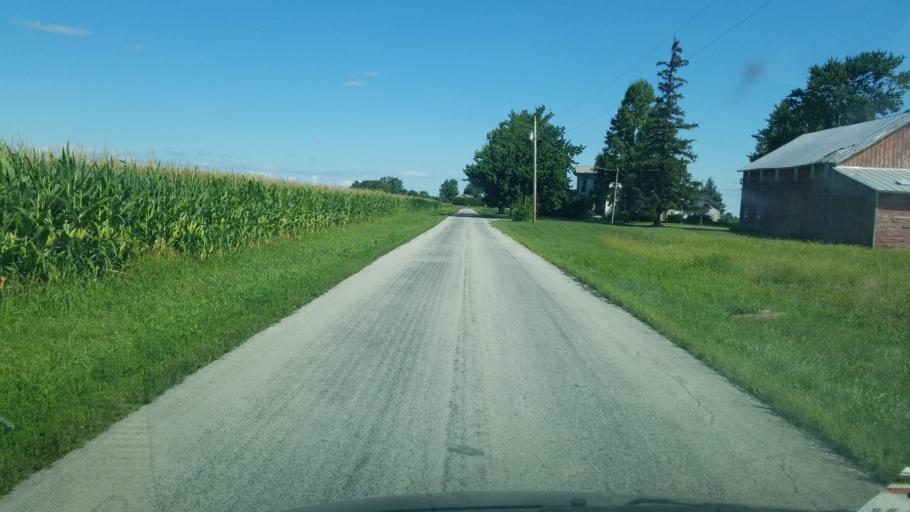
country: US
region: Ohio
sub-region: Hancock County
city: McComb
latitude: 41.1354
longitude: -83.7461
